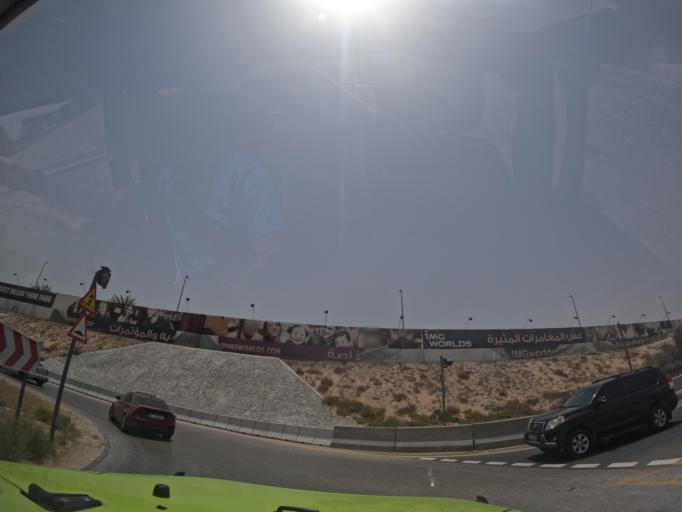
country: AE
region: Dubai
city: Dubai
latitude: 25.0900
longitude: 55.3249
